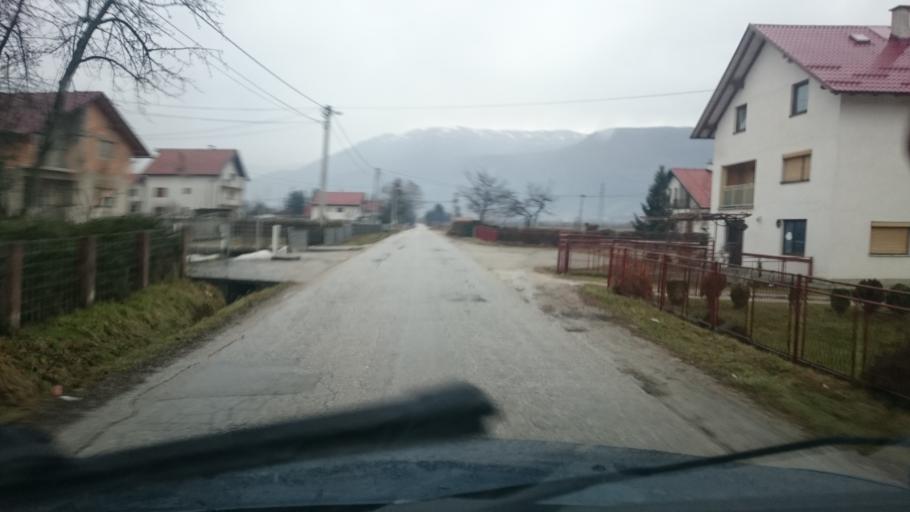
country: BA
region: Federation of Bosnia and Herzegovina
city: Travnik
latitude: 44.2006
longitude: 17.7036
